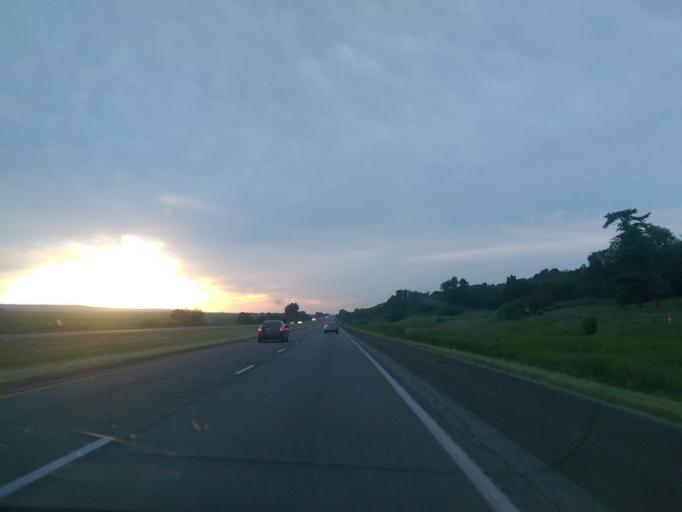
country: US
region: Missouri
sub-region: Holt County
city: Mound City
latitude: 40.2140
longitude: -95.3813
